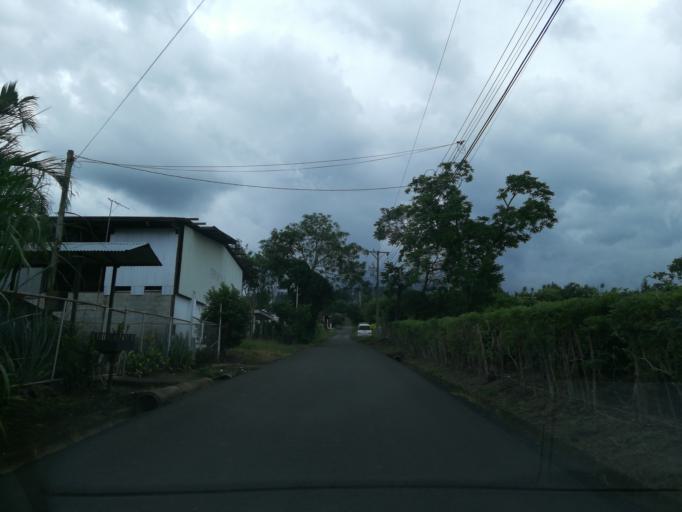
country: CR
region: Alajuela
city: Alajuela
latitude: 10.0364
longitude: -84.1827
